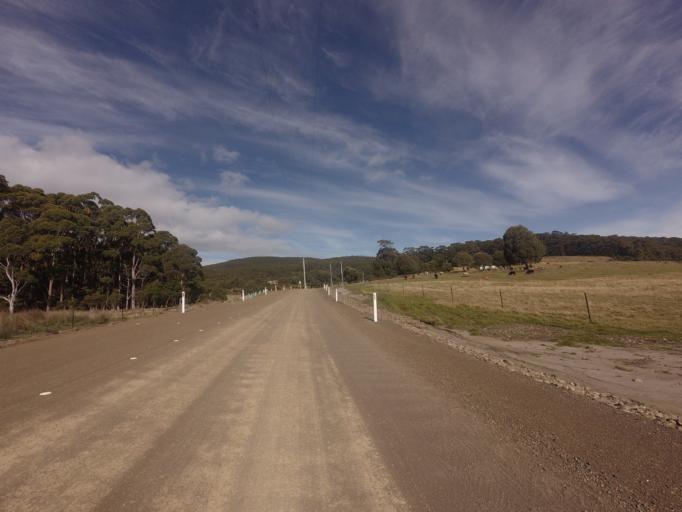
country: AU
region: Tasmania
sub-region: Clarence
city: Sandford
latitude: -43.1921
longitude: 147.7774
